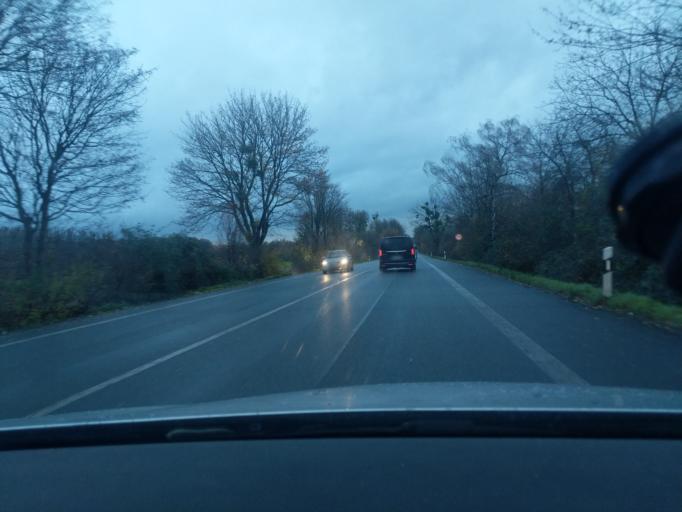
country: DE
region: North Rhine-Westphalia
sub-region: Regierungsbezirk Arnsberg
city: Hamm
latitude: 51.6331
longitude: 7.8458
